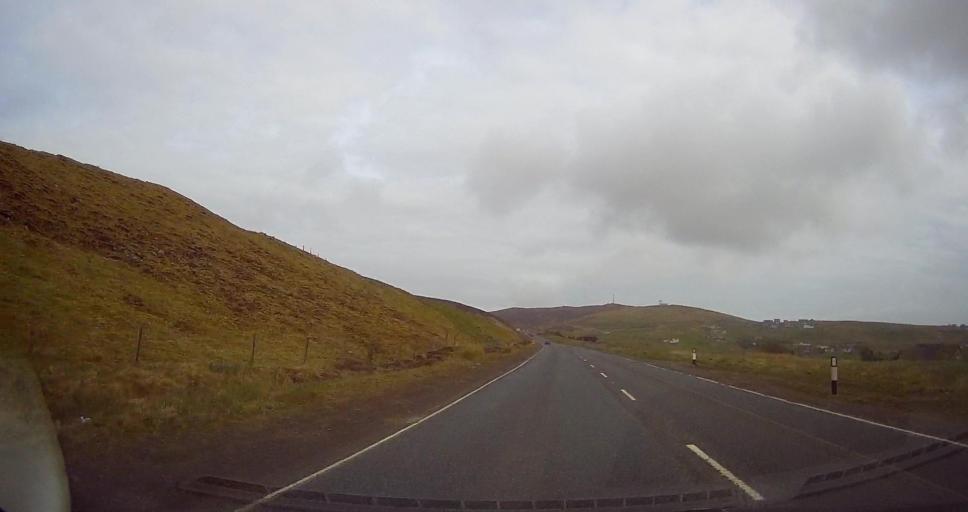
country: GB
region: Scotland
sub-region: Shetland Islands
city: Lerwick
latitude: 60.1280
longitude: -1.2160
